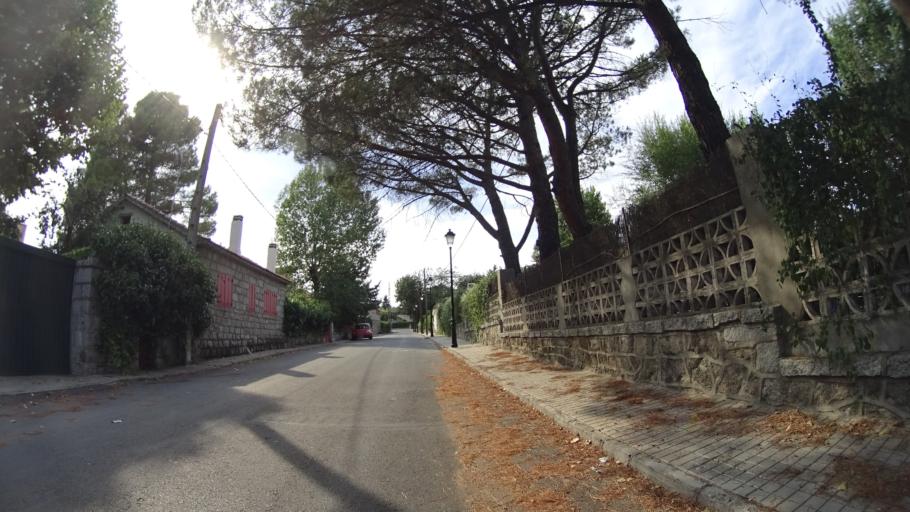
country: ES
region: Madrid
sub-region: Provincia de Madrid
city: Becerril de la Sierra
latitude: 40.7065
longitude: -3.9937
